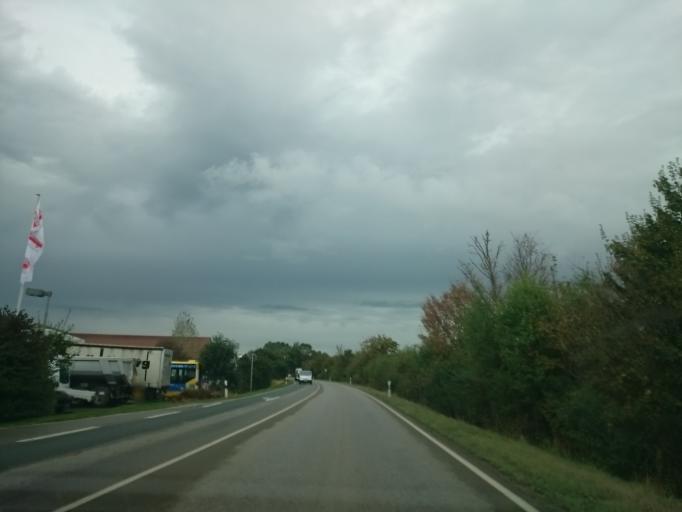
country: DE
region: Bavaria
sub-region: Swabia
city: Konigsbrunn
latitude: 48.2551
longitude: 10.8773
